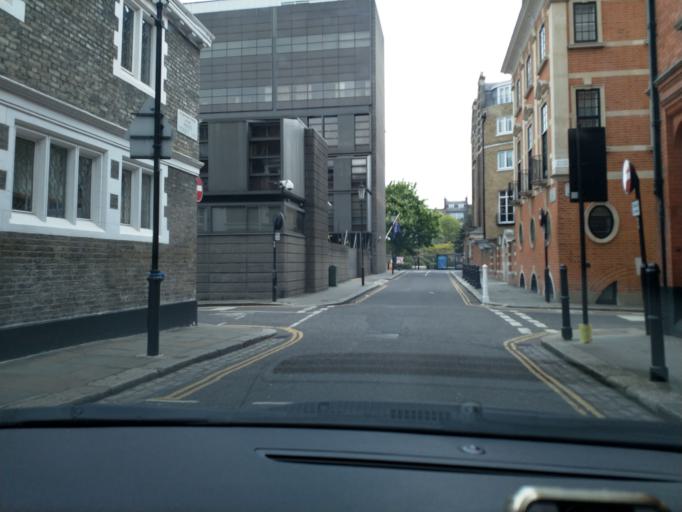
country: GB
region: England
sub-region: Greater London
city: Chelsea
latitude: 51.4976
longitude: -0.1601
